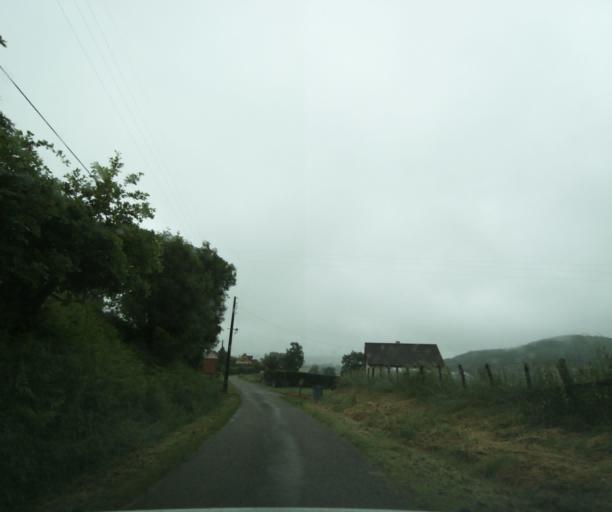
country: FR
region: Bourgogne
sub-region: Departement de Saone-et-Loire
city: Charolles
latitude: 46.4014
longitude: 4.3768
